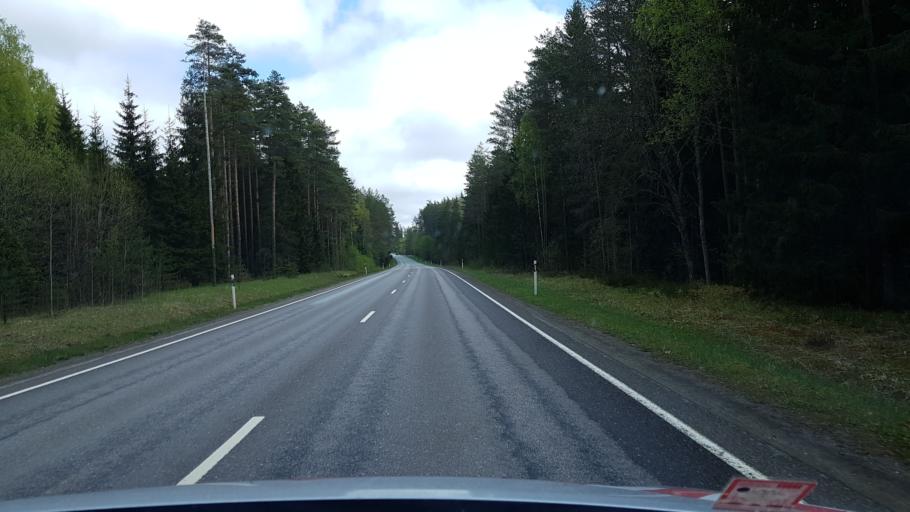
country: EE
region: Viljandimaa
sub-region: Moisakuela linn
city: Moisakula
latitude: 58.2471
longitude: 25.1579
